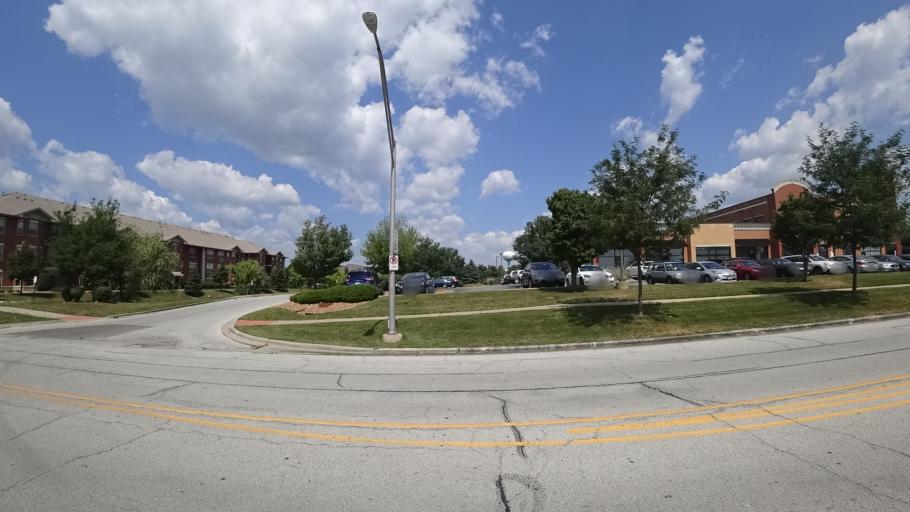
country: US
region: Illinois
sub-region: Cook County
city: Tinley Park
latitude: 41.6059
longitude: -87.7956
